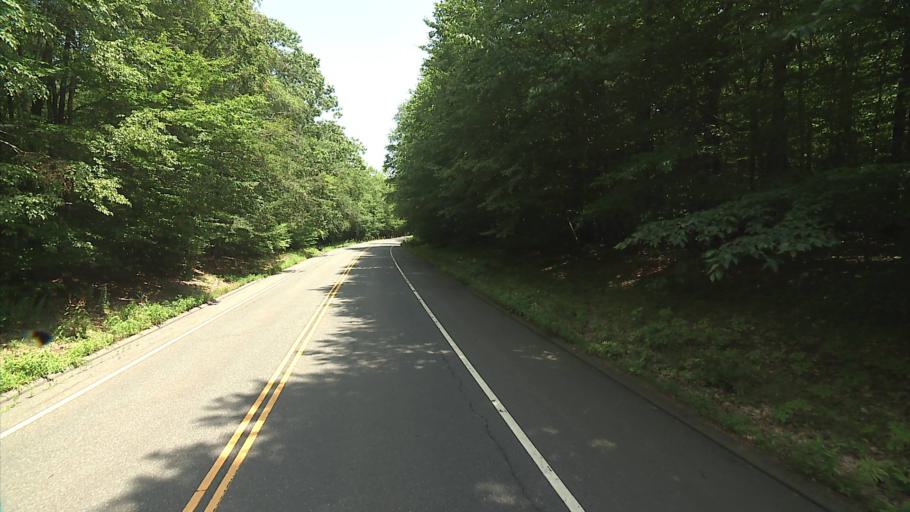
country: US
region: Massachusetts
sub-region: Hampden County
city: Granville
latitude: 42.0276
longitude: -72.9595
